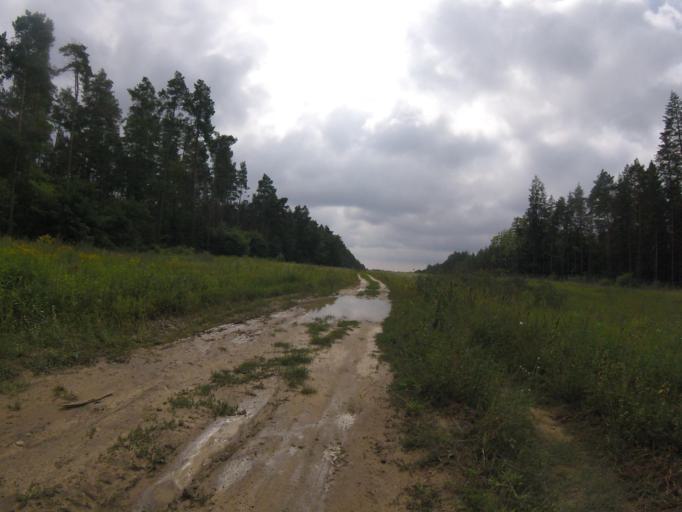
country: DE
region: Brandenburg
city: Gross Koris
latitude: 52.2066
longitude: 13.6506
